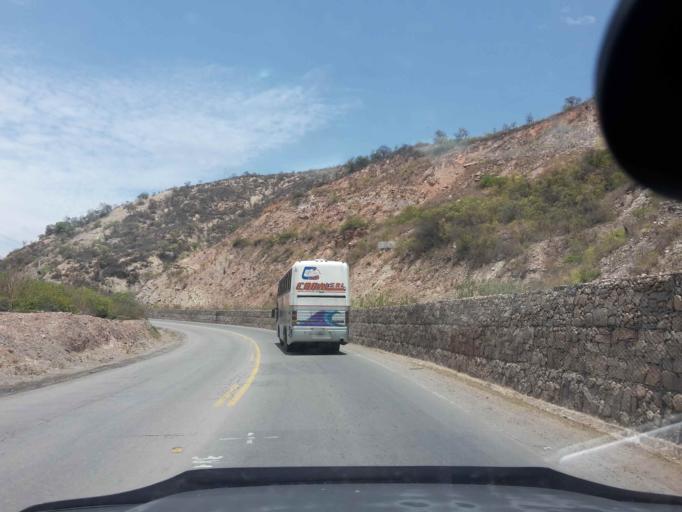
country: BO
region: Cochabamba
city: Sipe Sipe
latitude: -17.5355
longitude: -66.3357
